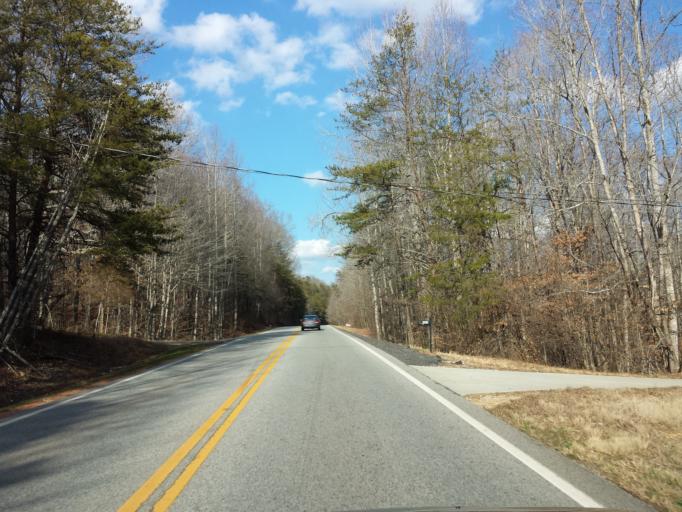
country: US
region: Georgia
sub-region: Lumpkin County
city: Dahlonega
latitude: 34.5132
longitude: -83.9233
